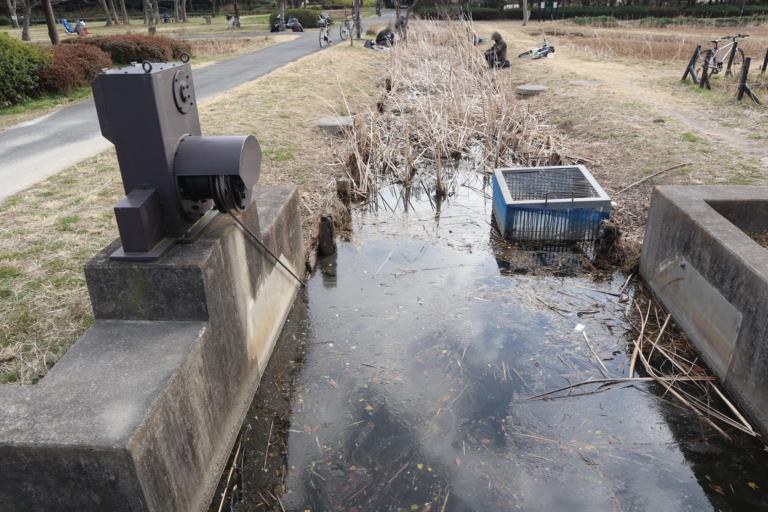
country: JP
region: Chiba
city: Matsudo
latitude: 35.7968
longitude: 139.8715
